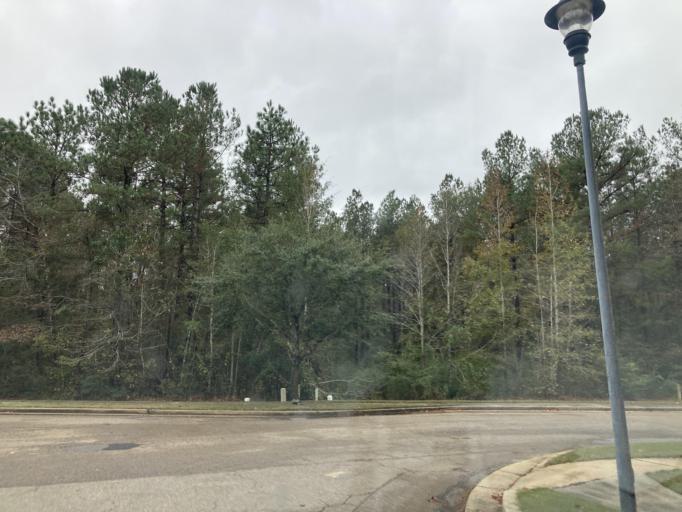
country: US
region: Mississippi
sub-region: Lamar County
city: West Hattiesburg
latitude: 31.2859
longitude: -89.4788
